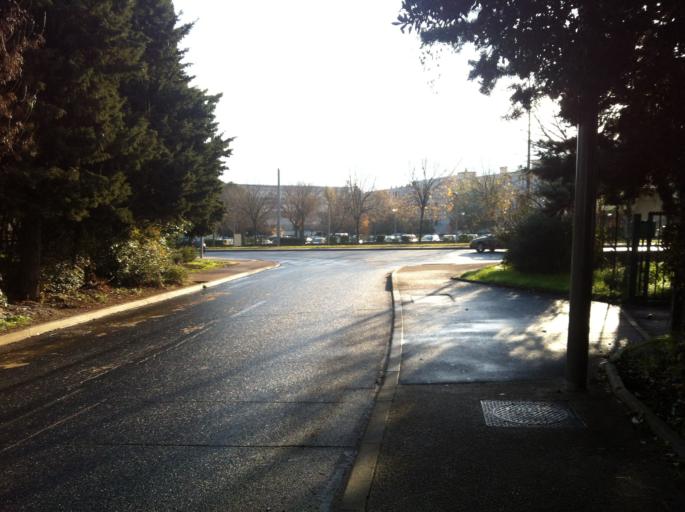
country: FR
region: Languedoc-Roussillon
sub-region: Departement de l'Herault
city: Montferrier-sur-Lez
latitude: 43.6358
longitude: 3.8452
